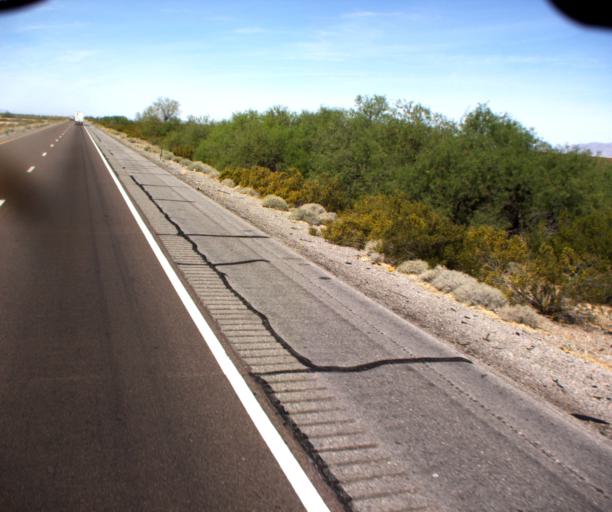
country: US
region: Arizona
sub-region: La Paz County
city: Salome
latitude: 33.5621
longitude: -113.3054
